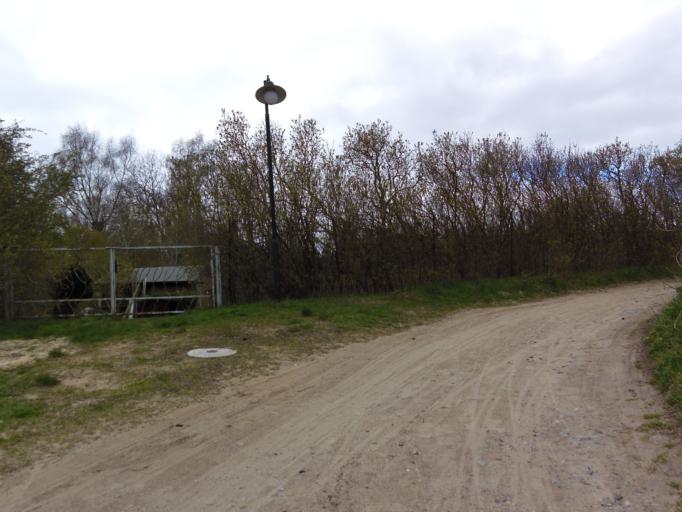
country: DE
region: Mecklenburg-Vorpommern
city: Hiddensee
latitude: 54.5877
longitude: 13.1105
